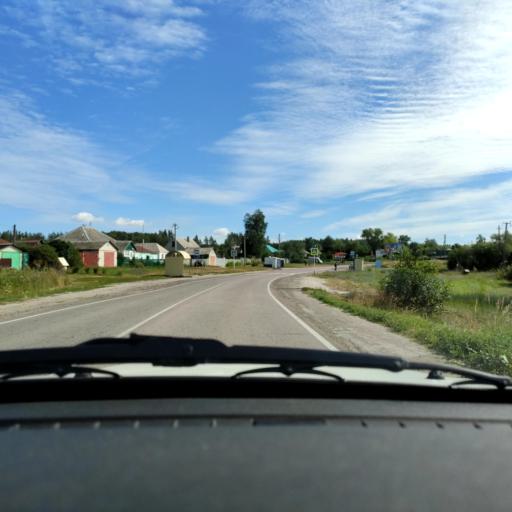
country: RU
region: Voronezj
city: Uglyanets
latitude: 51.8582
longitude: 39.6706
